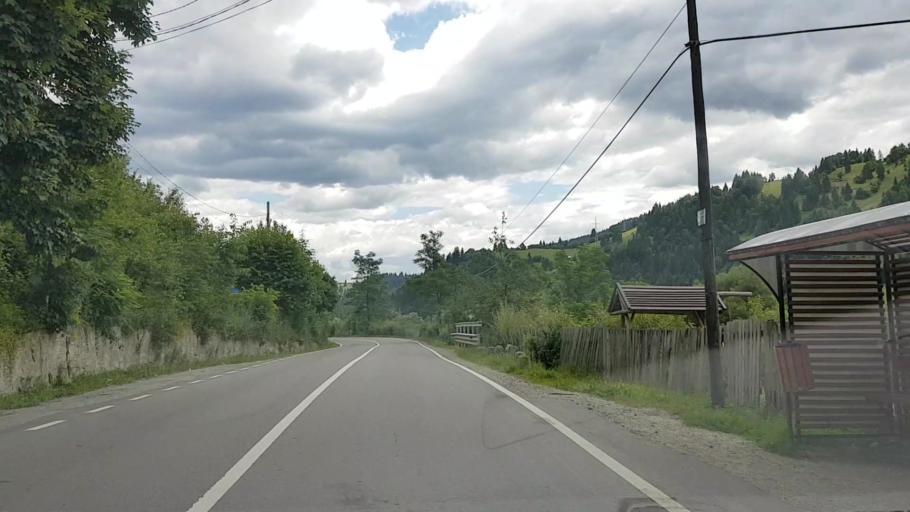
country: RO
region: Neamt
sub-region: Comuna Farcasa
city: Farcasa
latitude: 47.1599
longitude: 25.8227
